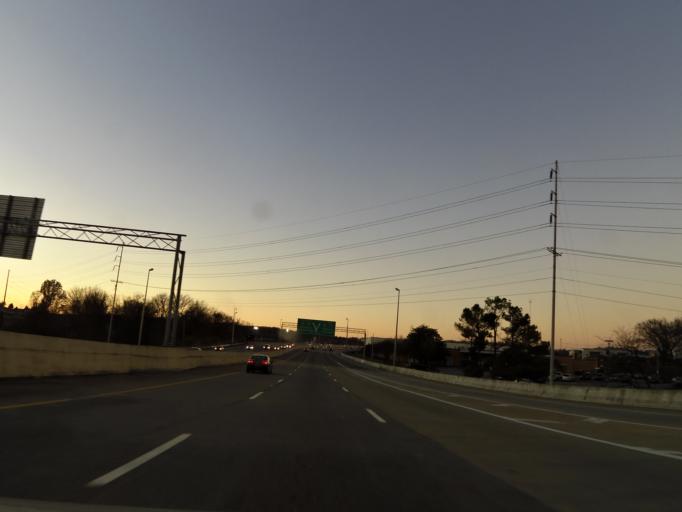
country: US
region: Tennessee
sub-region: Knox County
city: Knoxville
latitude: 35.9542
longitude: -83.9436
